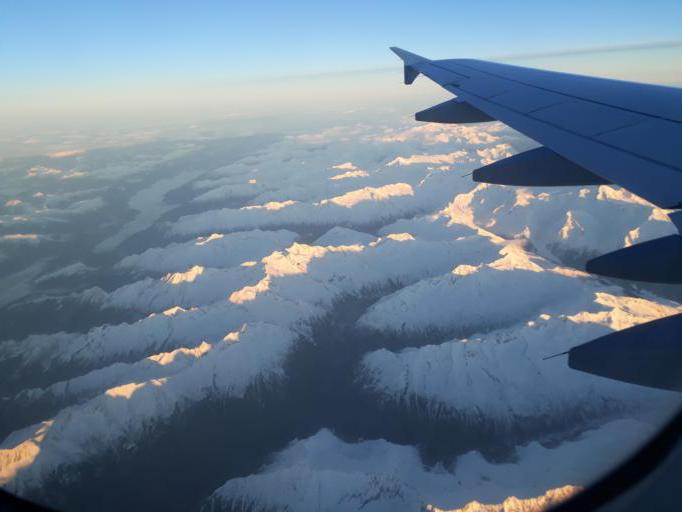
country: AT
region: Tyrol
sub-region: Politischer Bezirk Schwaz
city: Mayrhofen
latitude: 47.1025
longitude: 11.8744
